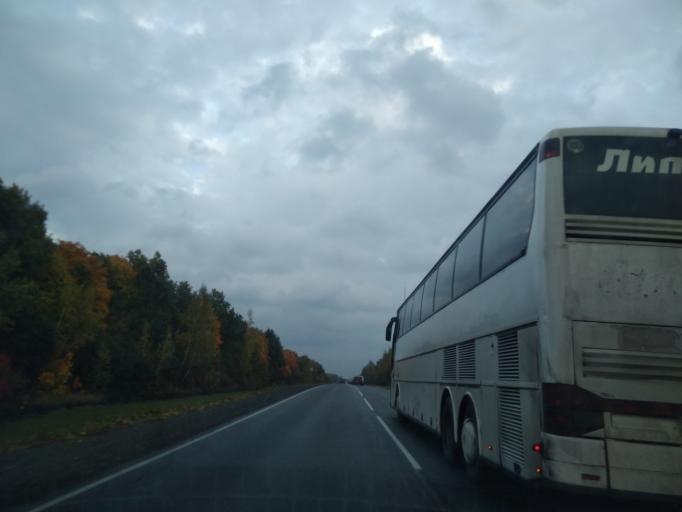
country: RU
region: Lipetsk
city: Borinskoye
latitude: 52.6002
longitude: 39.3238
